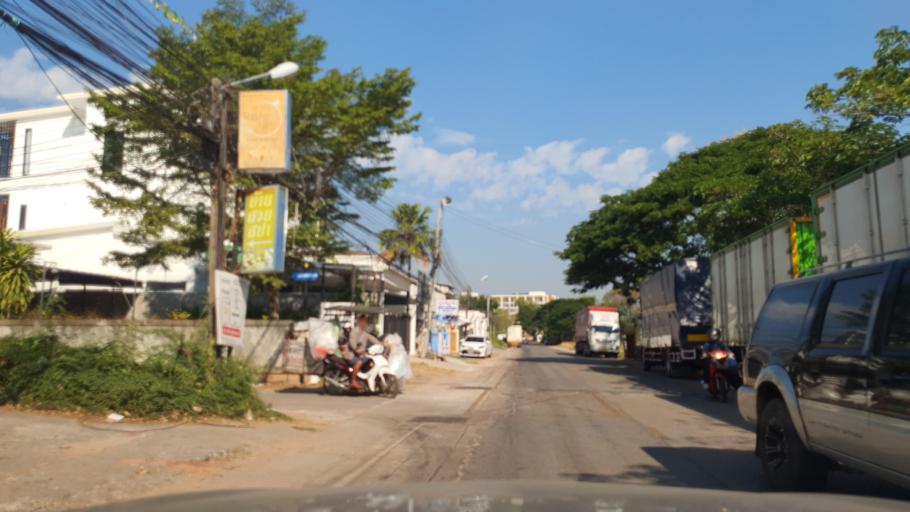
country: TH
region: Khon Kaen
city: Khon Kaen
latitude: 16.4363
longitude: 102.8142
